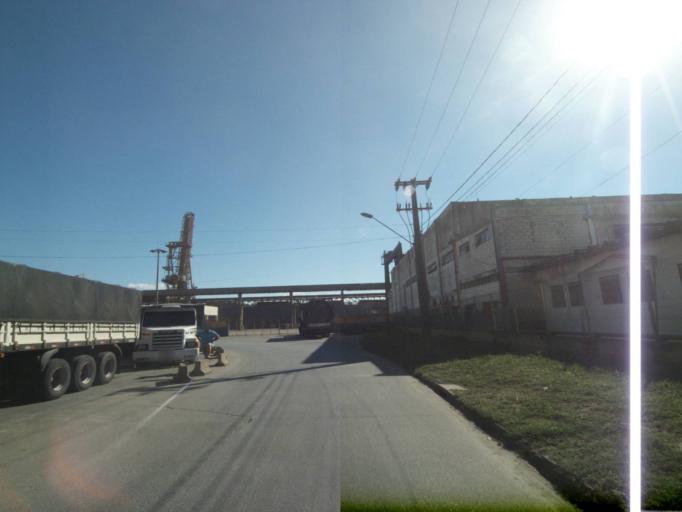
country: BR
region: Parana
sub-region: Paranagua
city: Paranagua
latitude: -25.5031
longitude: -48.5041
